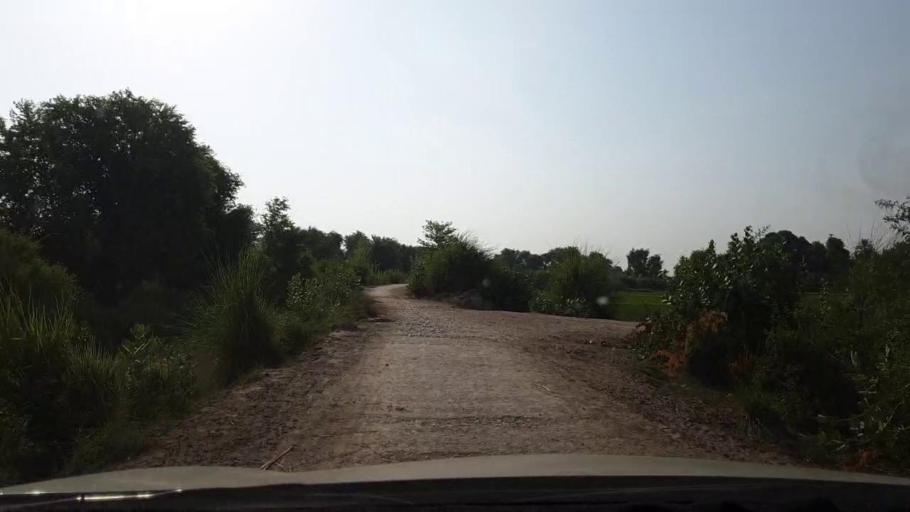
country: PK
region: Sindh
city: Larkana
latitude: 27.5508
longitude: 68.2649
